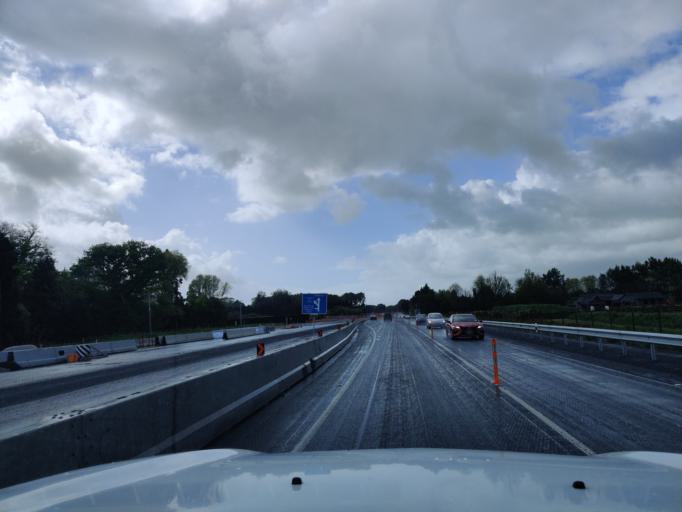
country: NZ
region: Waikato
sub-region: Hamilton City
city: Hamilton
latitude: -37.8214
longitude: 175.3483
